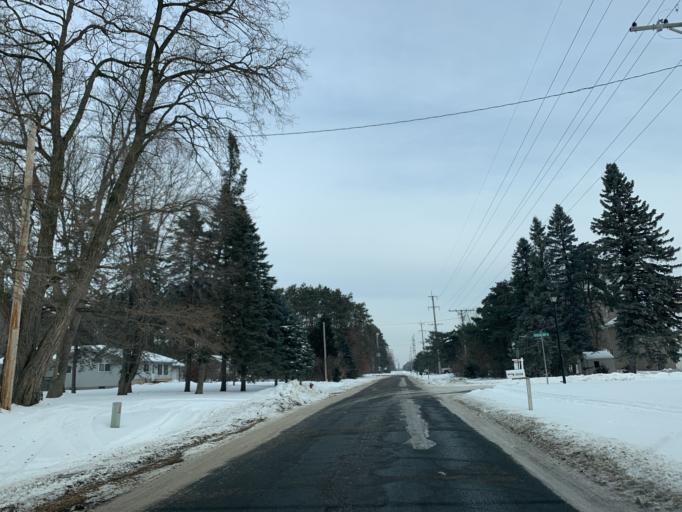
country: US
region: Minnesota
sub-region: Washington County
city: Forest Lake
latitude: 45.2846
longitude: -93.0090
